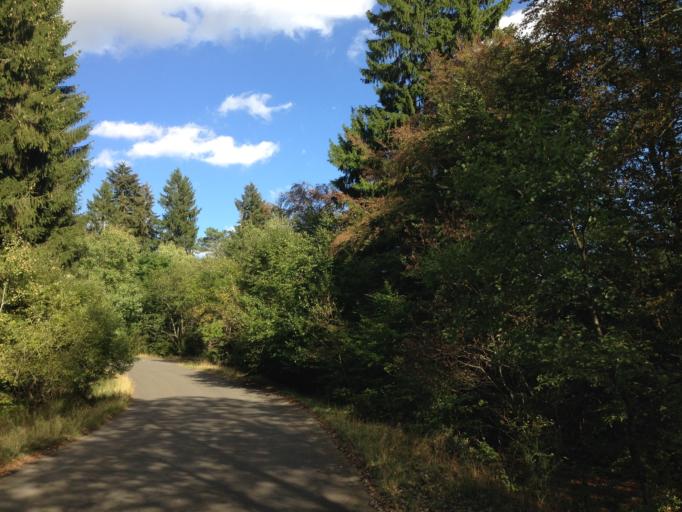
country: DE
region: Hesse
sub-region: Regierungsbezirk Giessen
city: Bad Endbach
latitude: 50.6684
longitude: 8.5476
